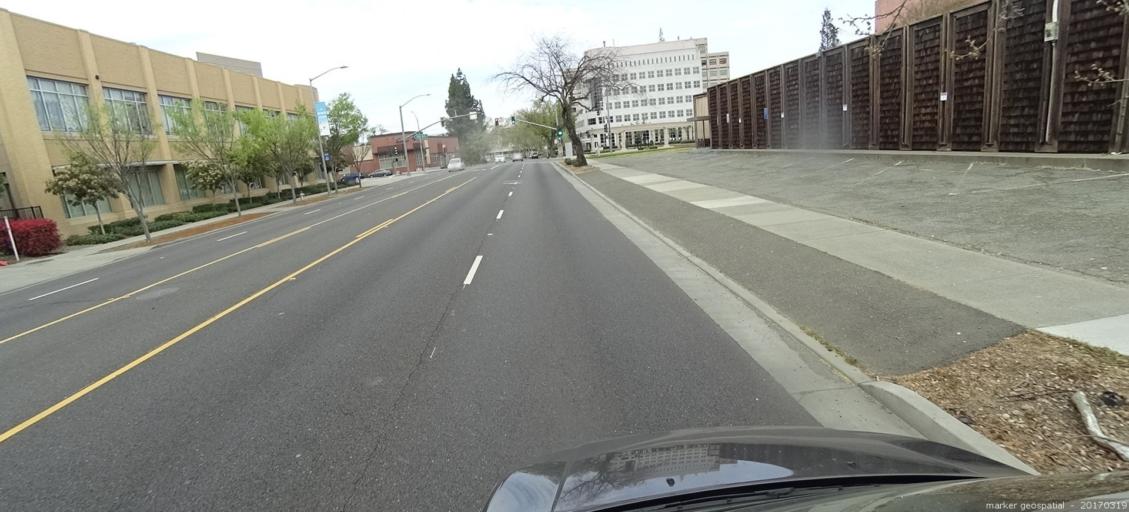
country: US
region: California
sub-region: Sacramento County
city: Sacramento
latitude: 38.5503
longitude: -121.4551
